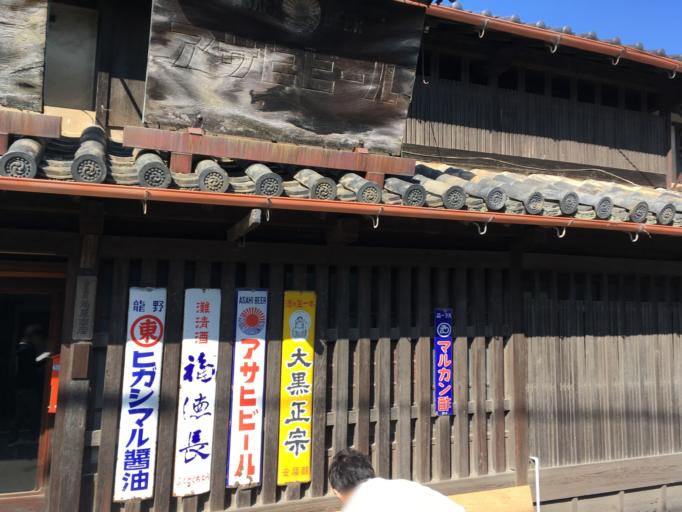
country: JP
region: Hyogo
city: Tatsunocho-tominaga
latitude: 34.8643
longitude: 134.5439
